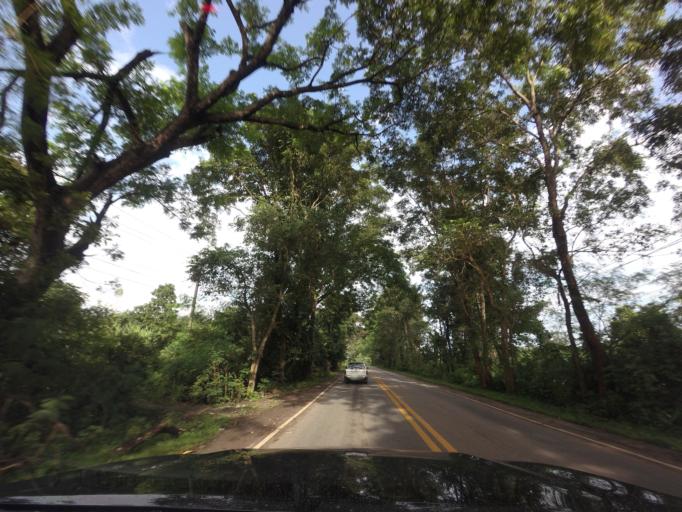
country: TH
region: Nong Khai
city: Pho Tak
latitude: 17.7839
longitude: 102.3742
